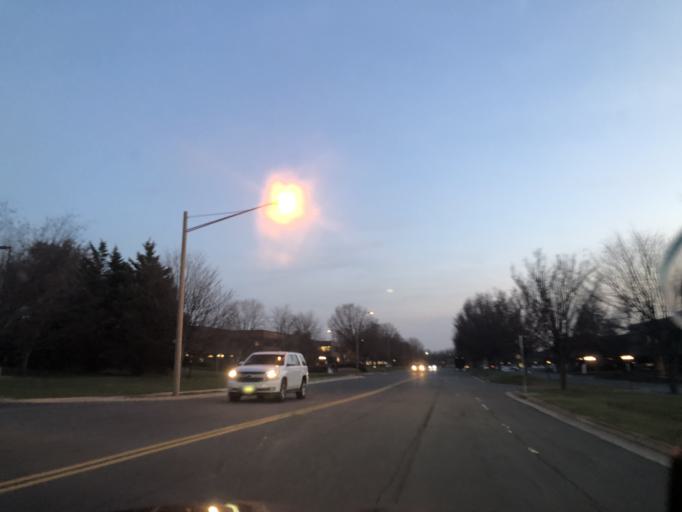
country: US
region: Virginia
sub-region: Loudoun County
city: Leesburg
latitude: 39.0841
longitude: -77.5565
